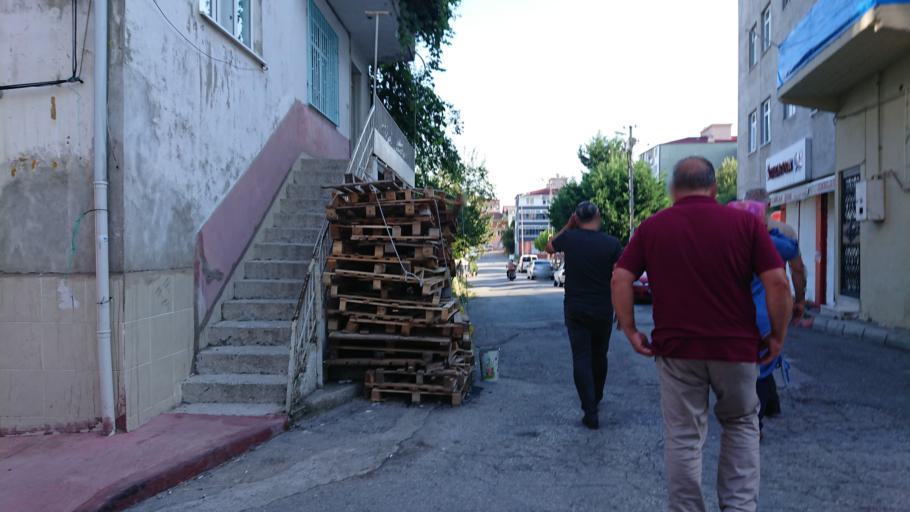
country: TR
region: Samsun
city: Samsun
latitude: 41.2995
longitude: 36.3208
